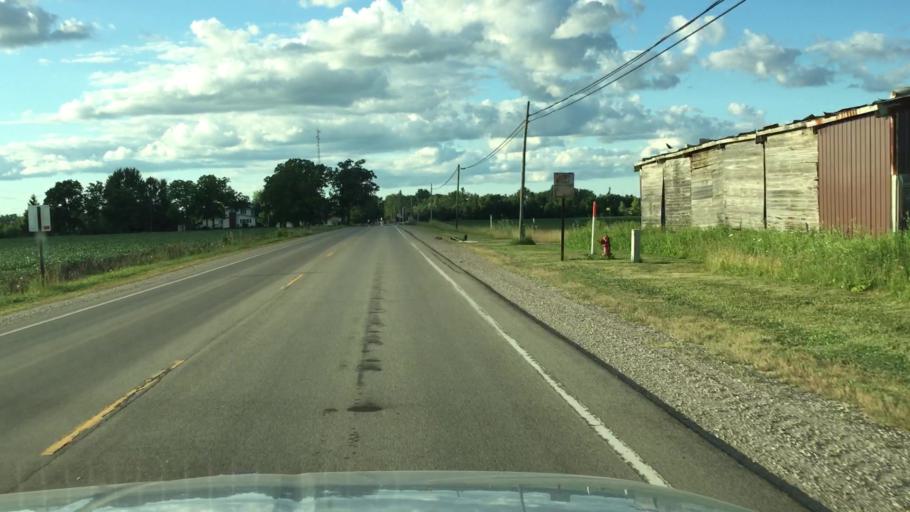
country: US
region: Michigan
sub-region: Saint Clair County
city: Capac
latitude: 43.0006
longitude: -82.9282
